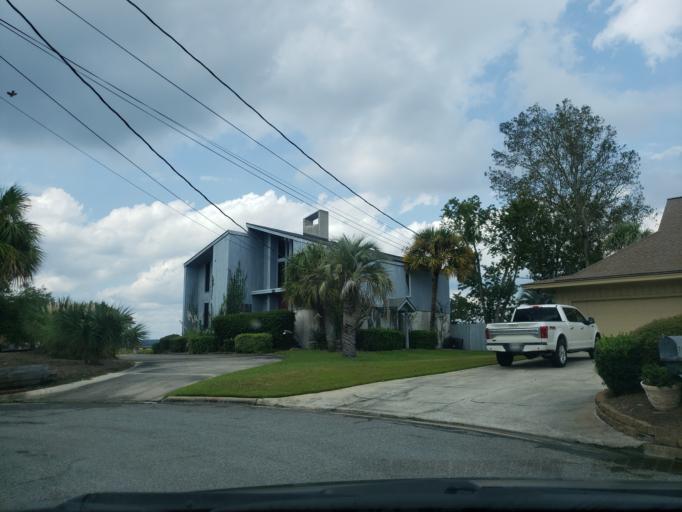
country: US
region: Georgia
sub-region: Chatham County
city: Skidaway Island
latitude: 31.9305
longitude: -81.0836
